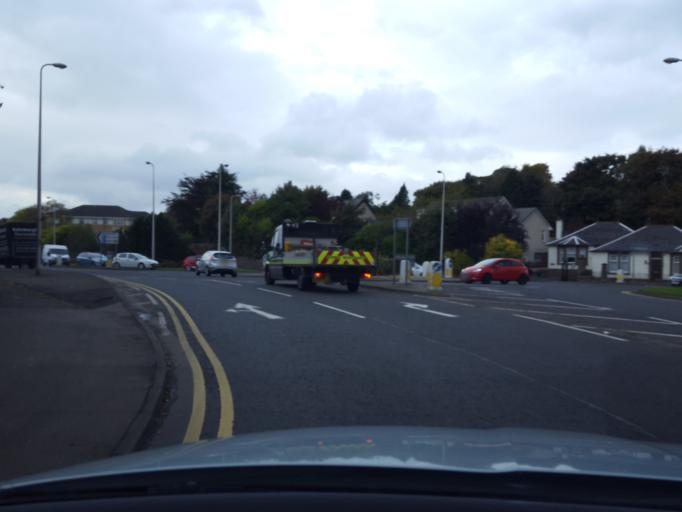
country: GB
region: Scotland
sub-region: West Lothian
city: Bathgate
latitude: 55.8946
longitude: -3.6230
